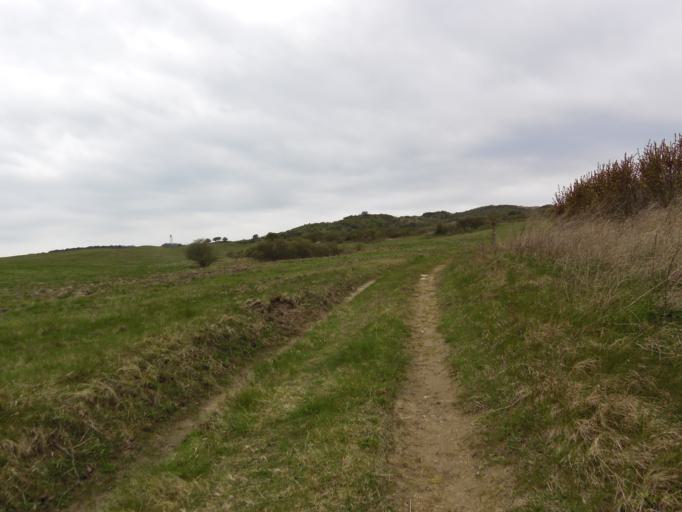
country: DE
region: Mecklenburg-Vorpommern
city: Hiddensee
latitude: 54.6017
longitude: 13.1395
